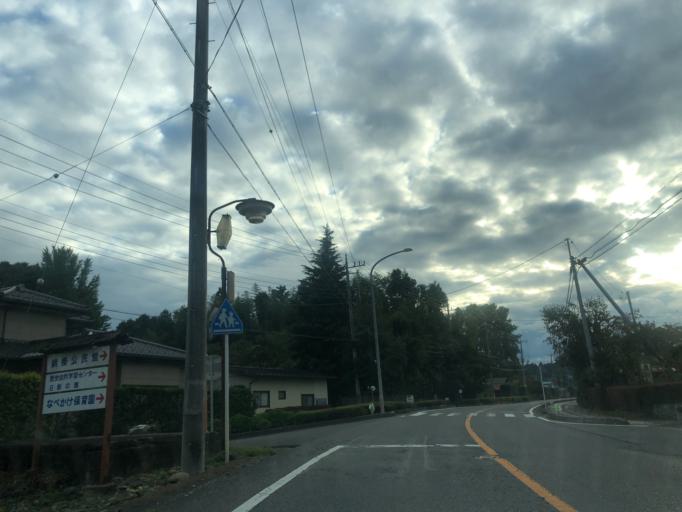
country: JP
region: Tochigi
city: Kuroiso
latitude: 36.9436
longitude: 140.1031
